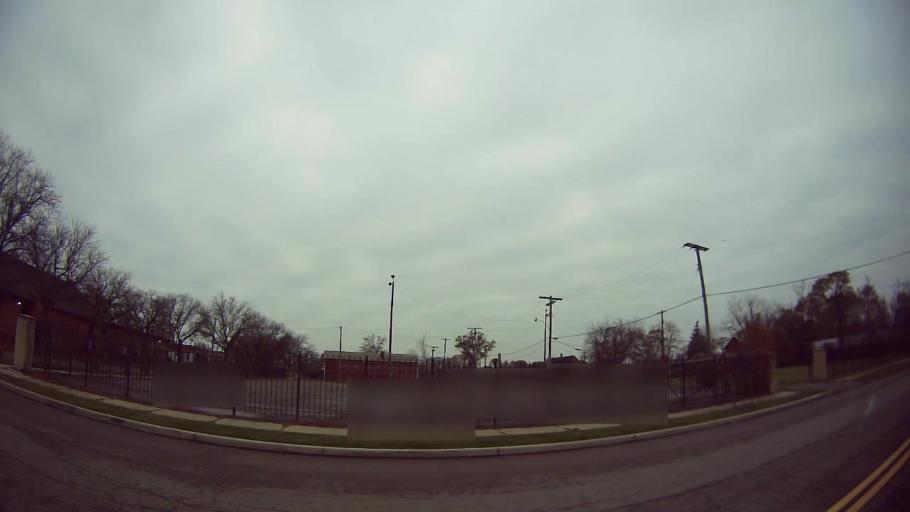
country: US
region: Michigan
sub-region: Wayne County
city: Highland Park
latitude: 42.4132
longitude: -83.0799
